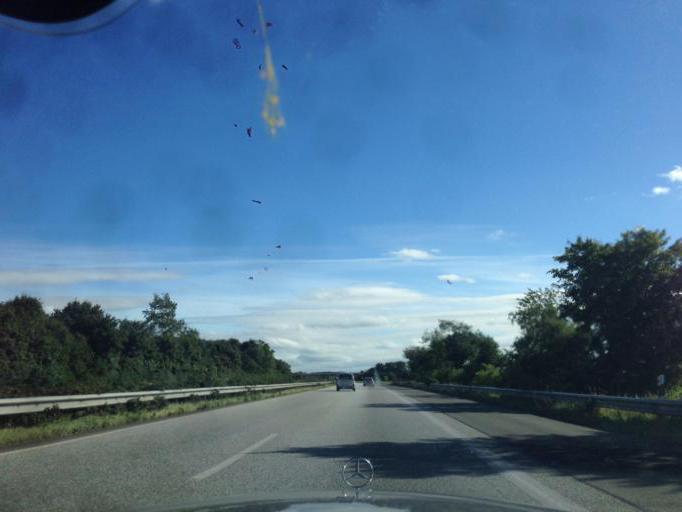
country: DE
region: Schleswig-Holstein
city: Schuby
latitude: 54.5382
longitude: 9.4724
